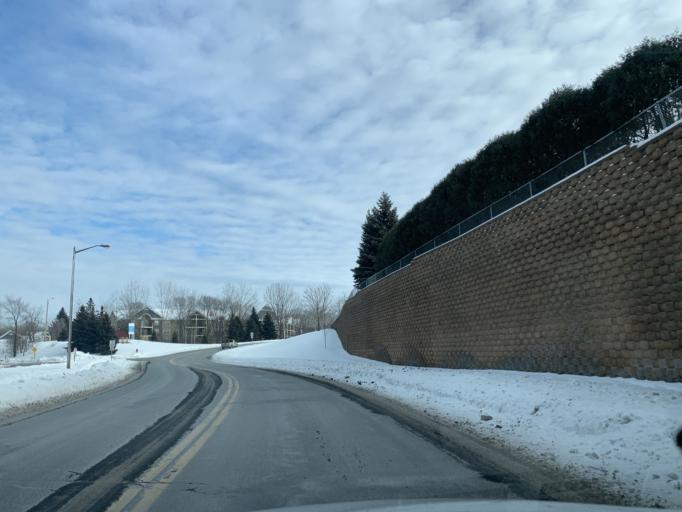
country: US
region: Minnesota
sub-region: Dakota County
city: Burnsville
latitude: 44.7506
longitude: -93.2820
